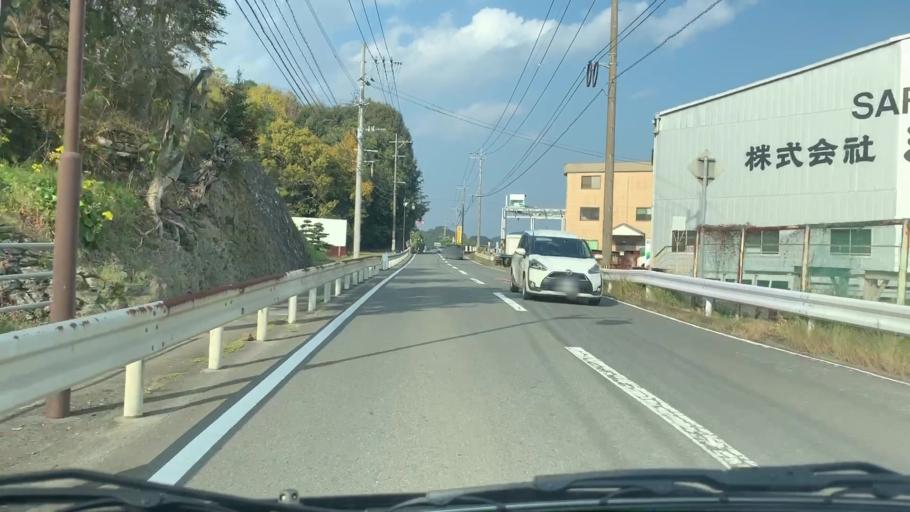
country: JP
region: Nagasaki
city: Togitsu
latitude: 32.9403
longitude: 129.7819
